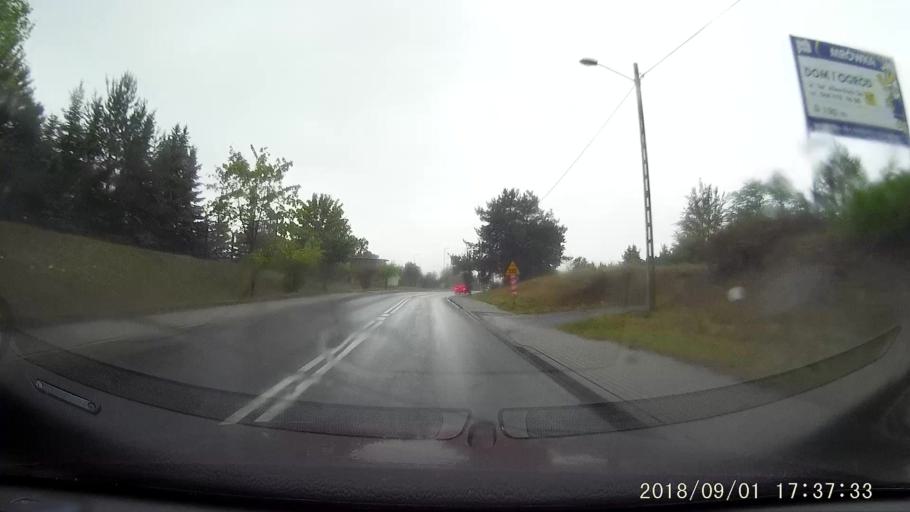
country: PL
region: Lubusz
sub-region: Powiat zaganski
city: Zagan
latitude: 51.6069
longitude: 15.3001
